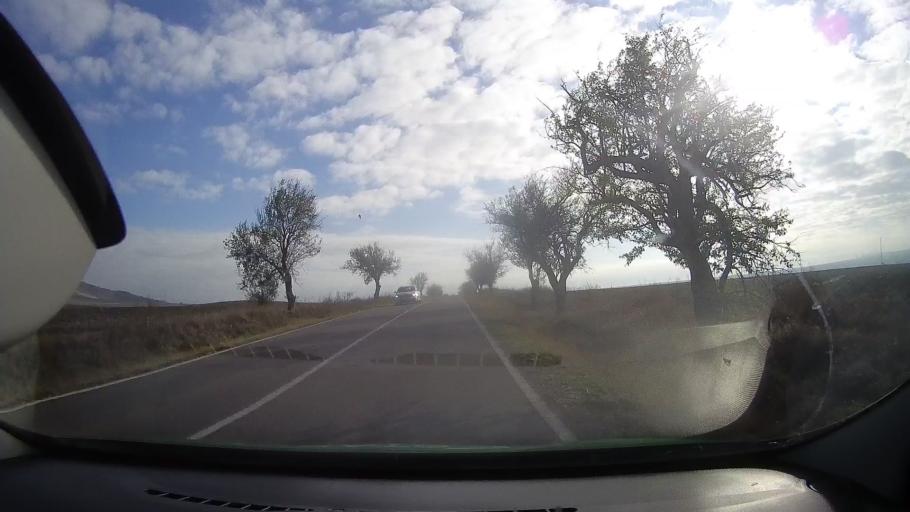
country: RO
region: Tulcea
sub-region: Comuna Bestepe
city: Bestepe
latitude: 45.0816
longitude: 29.0320
